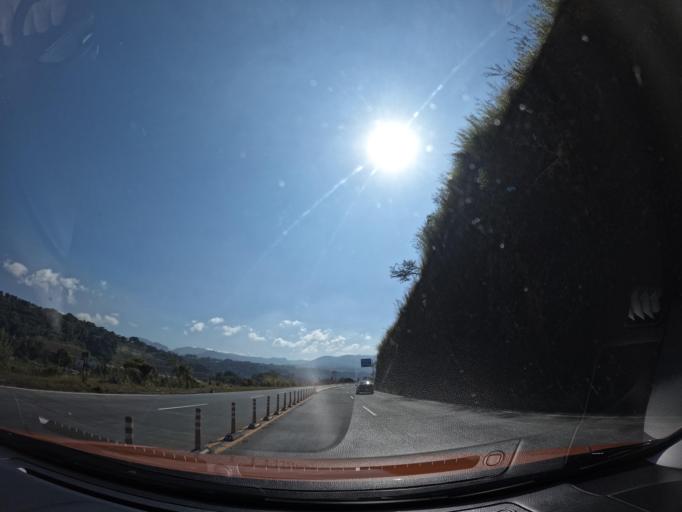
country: GT
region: Guatemala
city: Petapa
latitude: 14.4925
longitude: -90.5416
